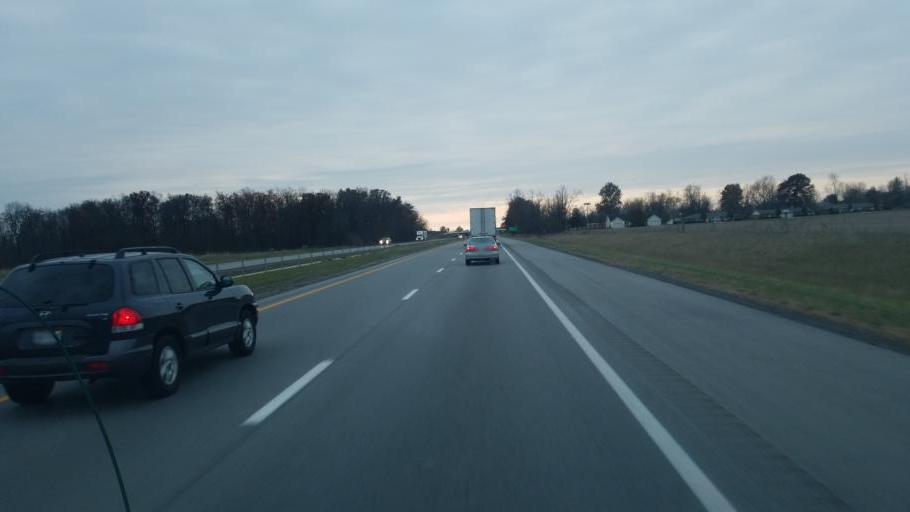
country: US
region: Ohio
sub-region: Auglaize County
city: Cridersville
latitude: 40.6619
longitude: -84.1316
